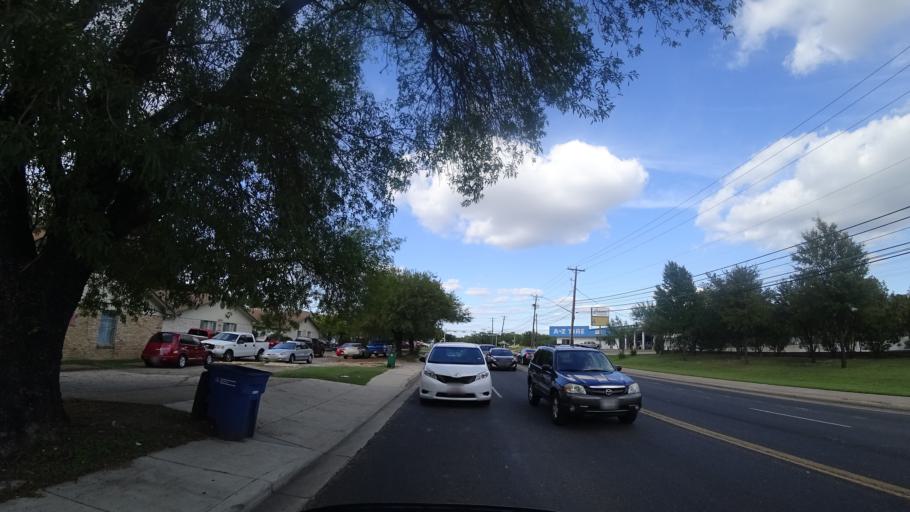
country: US
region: Texas
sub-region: Travis County
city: Onion Creek
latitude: 30.1995
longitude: -97.7864
